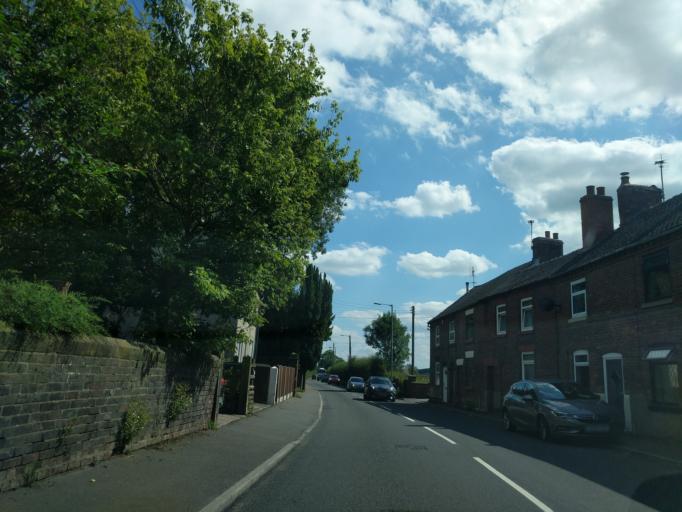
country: GB
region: England
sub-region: Staffordshire
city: Cheadle
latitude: 52.9517
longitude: -1.9848
